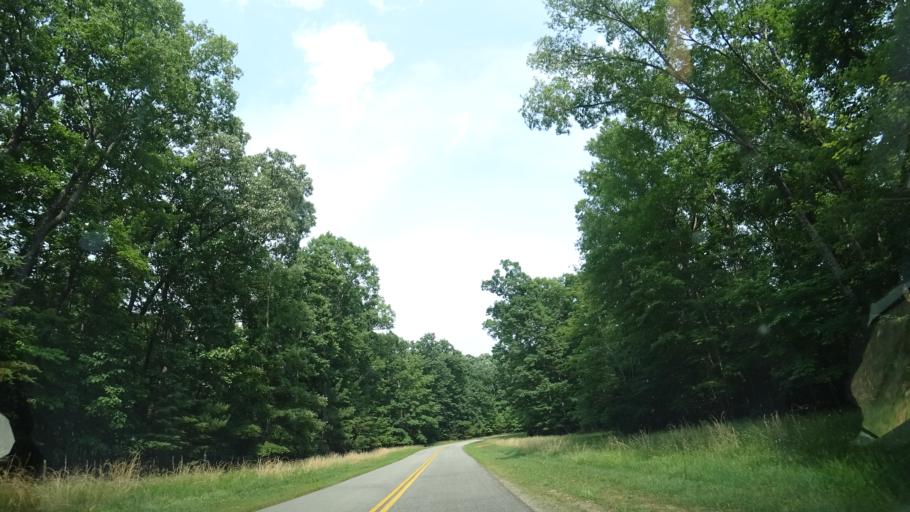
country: US
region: Virginia
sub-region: Louisa County
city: Louisa
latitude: 38.1176
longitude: -77.8202
